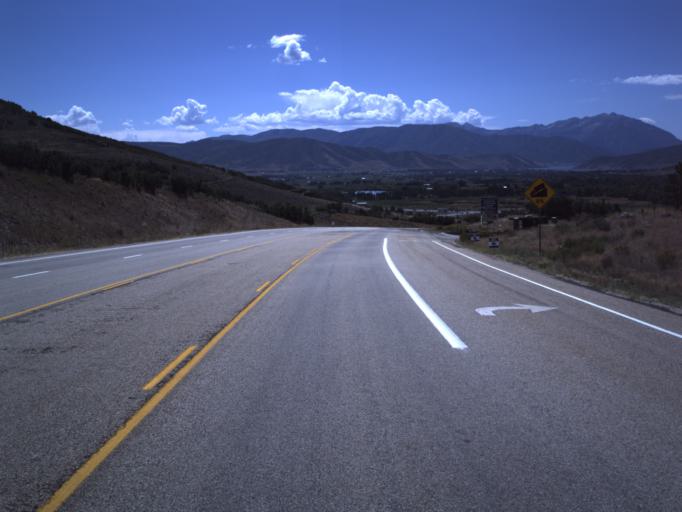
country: US
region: Utah
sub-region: Wasatch County
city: Heber
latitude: 40.5683
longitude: -111.4211
